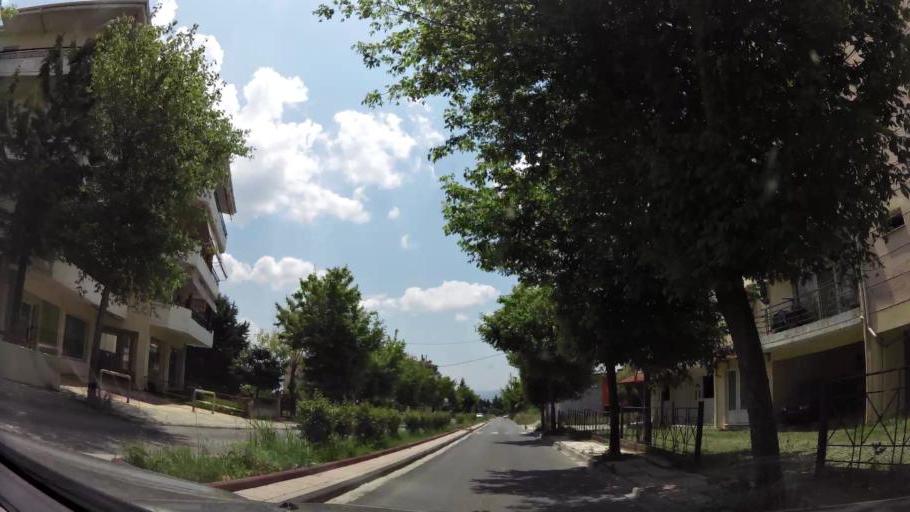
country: GR
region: West Macedonia
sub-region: Nomos Kozanis
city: Kozani
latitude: 40.2904
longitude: 21.7984
